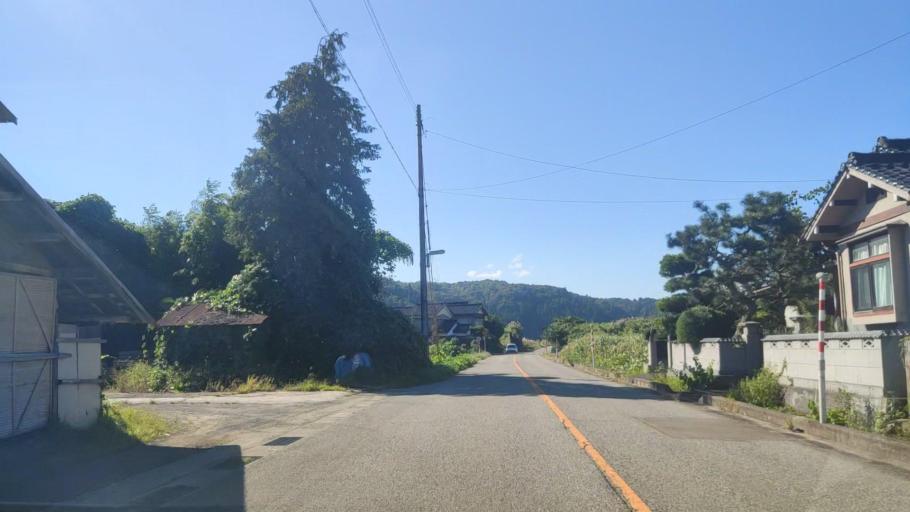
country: JP
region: Ishikawa
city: Nanao
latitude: 37.2566
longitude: 137.0792
